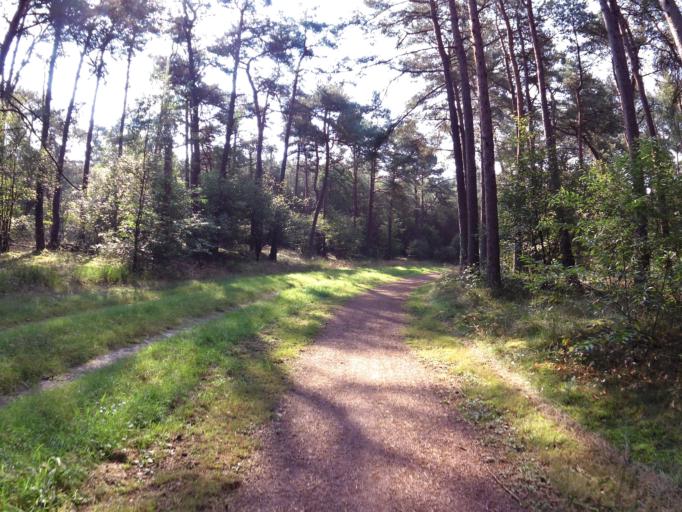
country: NL
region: Overijssel
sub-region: Gemeente Twenterand
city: Den Ham
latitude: 52.5023
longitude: 6.4514
